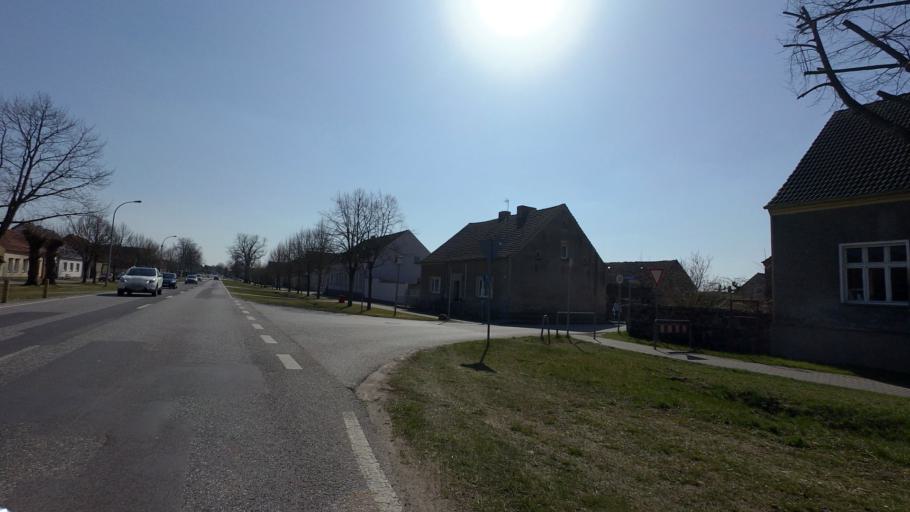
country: DE
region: Brandenburg
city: Oranienburg
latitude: 52.8534
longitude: 13.1732
